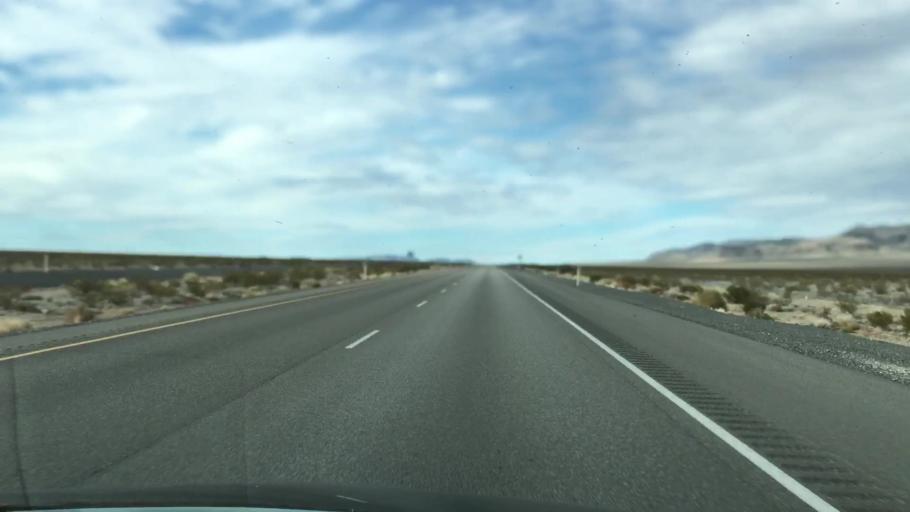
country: US
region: Nevada
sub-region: Nye County
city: Pahrump
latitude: 36.5796
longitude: -115.8933
